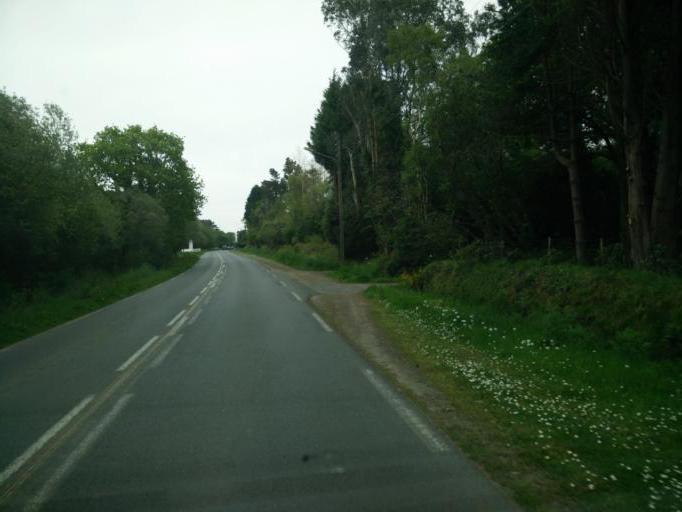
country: FR
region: Brittany
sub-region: Departement des Cotes-d'Armor
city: Trebeurden
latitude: 48.7626
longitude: -3.5439
